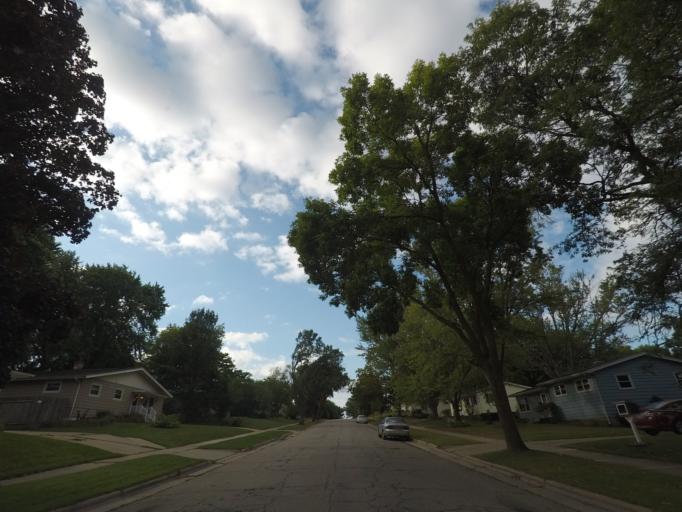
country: US
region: Wisconsin
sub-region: Dane County
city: Monona
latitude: 43.0762
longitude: -89.3022
